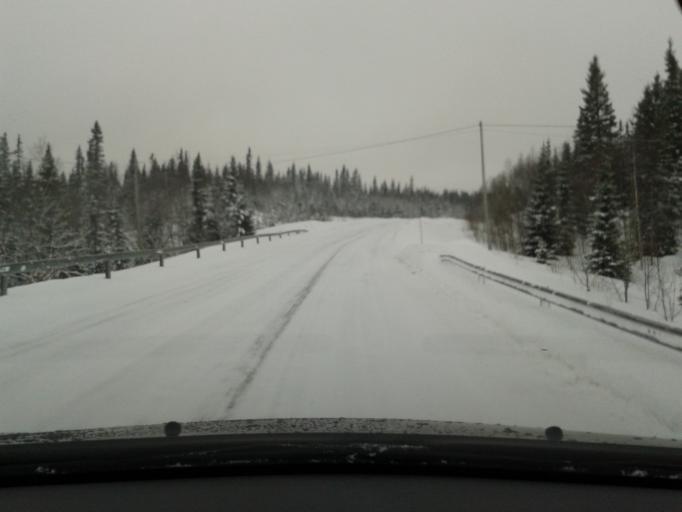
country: SE
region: Vaesterbotten
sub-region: Vilhelmina Kommun
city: Sjoberg
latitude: 65.1642
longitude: 15.8791
